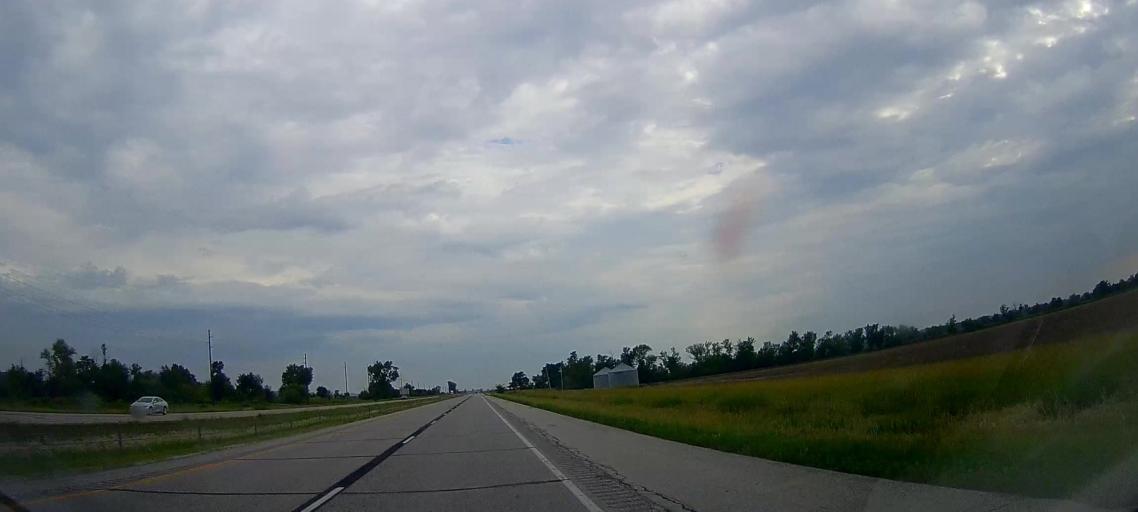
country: US
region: Iowa
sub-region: Harrison County
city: Missouri Valley
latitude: 41.4702
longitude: -95.8998
